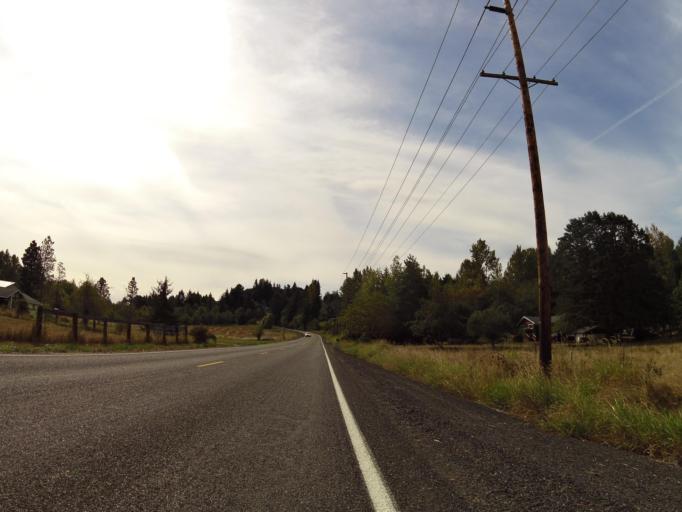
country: US
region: Washington
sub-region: Lewis County
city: Chehalis
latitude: 46.6384
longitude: -122.9714
